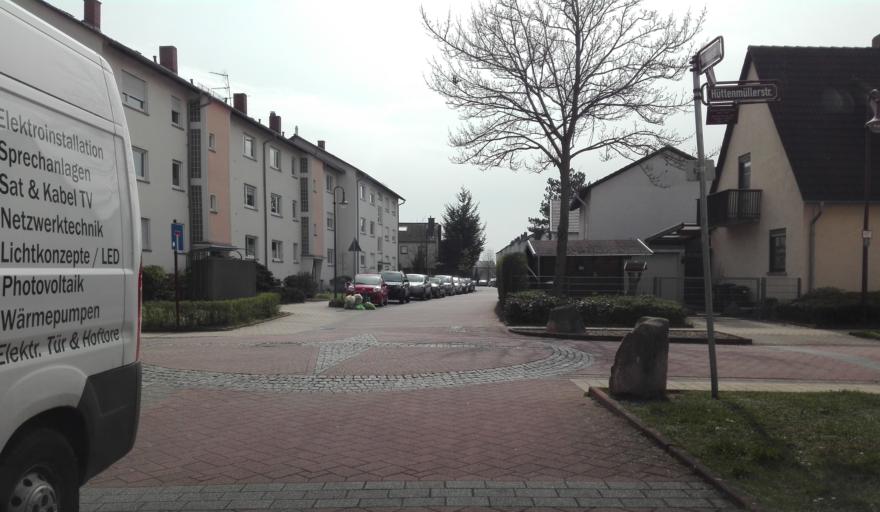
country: DE
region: Rheinland-Pfalz
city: Maxdorf
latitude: 49.4767
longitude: 8.2885
